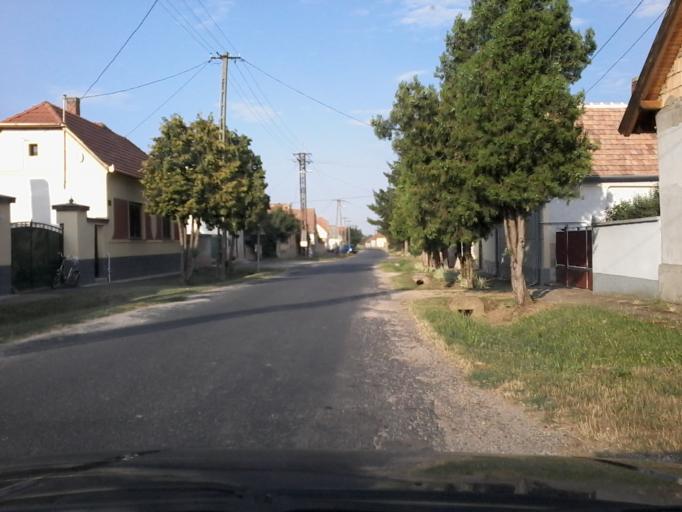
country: HU
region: Vas
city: Janoshaza
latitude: 47.0931
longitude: 17.1954
